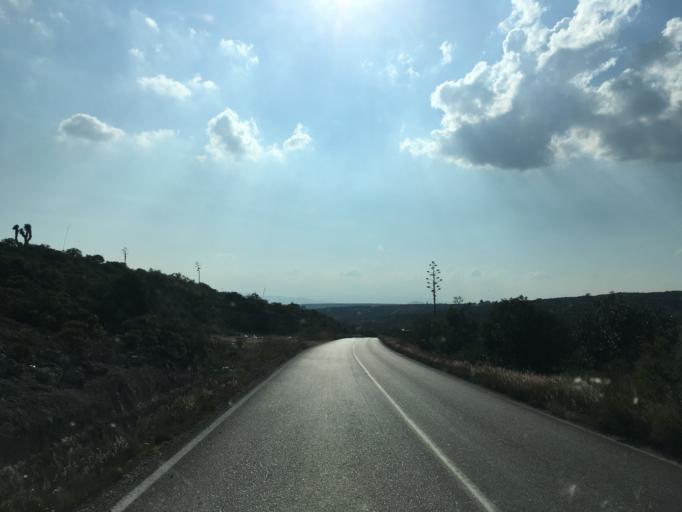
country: MX
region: Hidalgo
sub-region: Cardonal
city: Pozuelos
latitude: 20.6025
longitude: -99.1096
